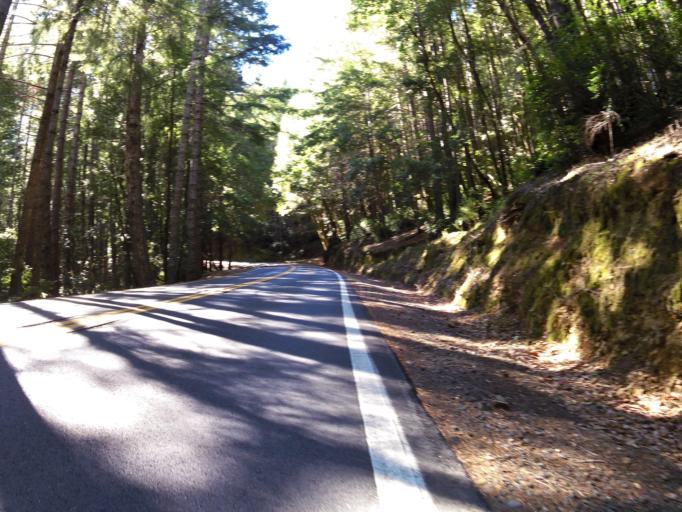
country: US
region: California
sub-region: Humboldt County
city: Redway
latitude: 39.8513
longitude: -123.7355
